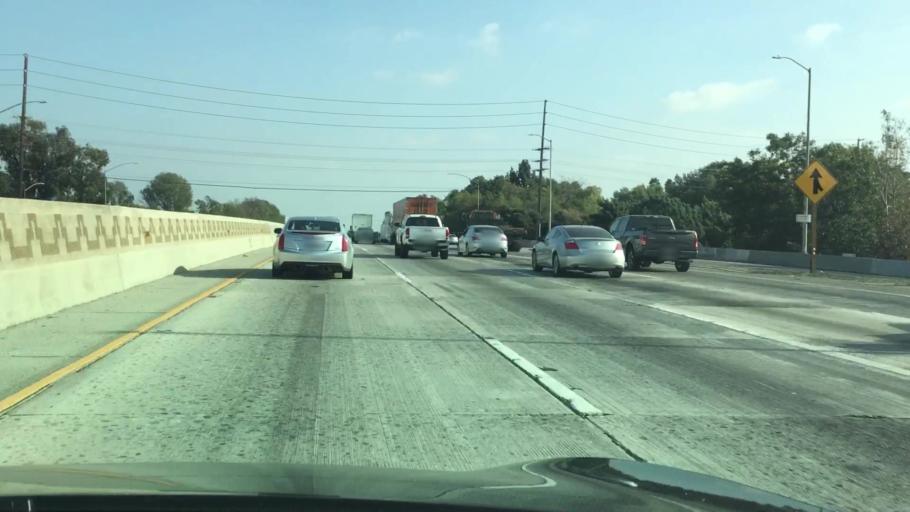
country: US
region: California
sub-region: Los Angeles County
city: Downey
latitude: 33.9583
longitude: -118.1125
